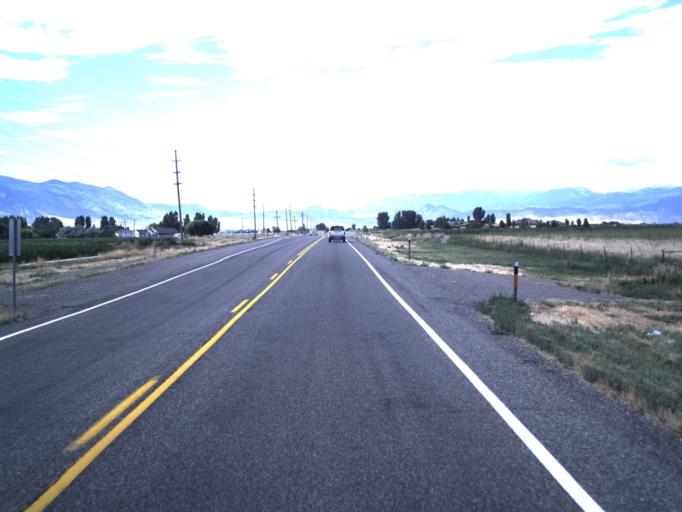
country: US
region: Utah
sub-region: Sevier County
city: Richfield
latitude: 38.7074
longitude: -112.1082
